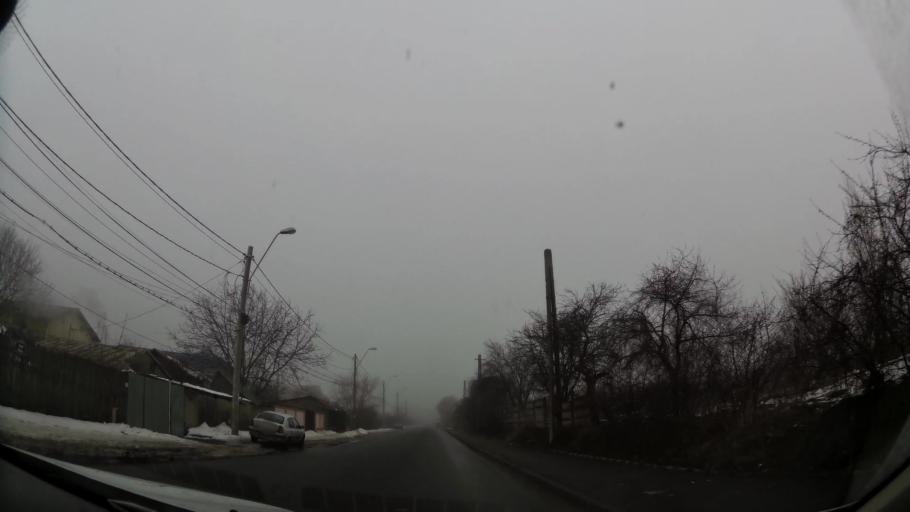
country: RO
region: Ilfov
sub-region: Comuna Chiajna
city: Rosu
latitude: 44.4746
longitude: 26.0128
